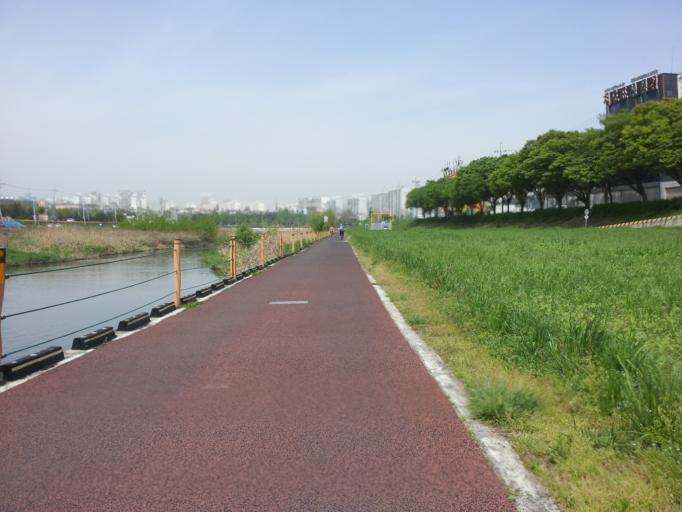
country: KR
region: Daejeon
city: Daejeon
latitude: 36.3488
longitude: 127.4087
